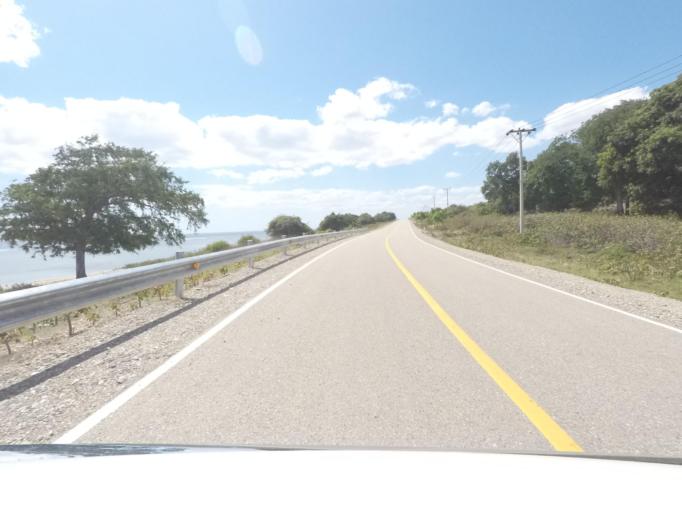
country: TL
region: Lautem
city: Lospalos
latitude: -8.4192
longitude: 126.7750
